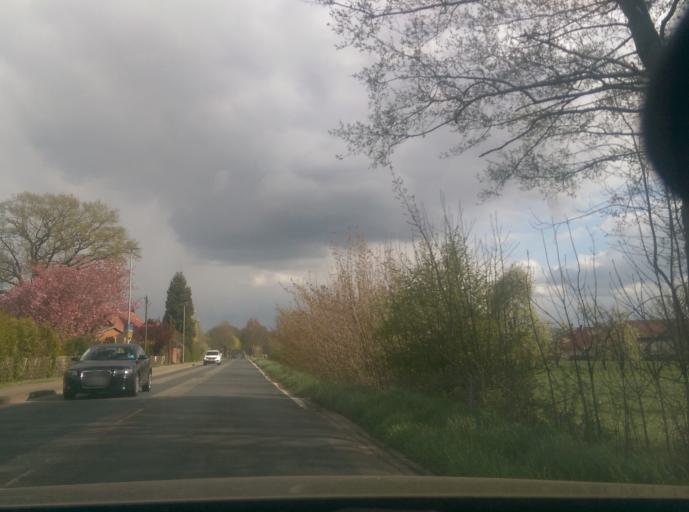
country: DE
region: Lower Saxony
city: Lindwedel
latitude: 52.5679
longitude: 9.6187
